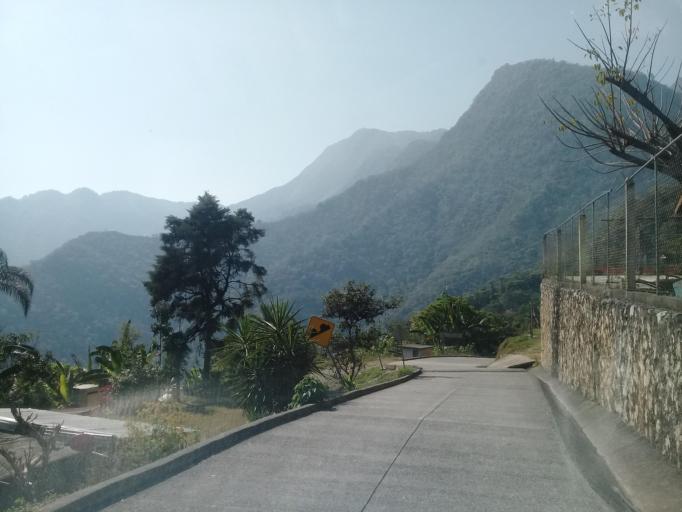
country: MX
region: Veracruz
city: Rafael Delgado
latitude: 18.7839
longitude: -97.0278
